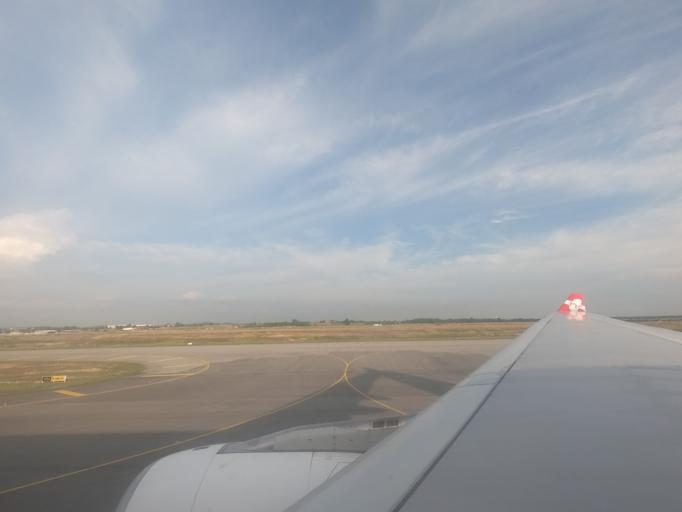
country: MY
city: Sungai Pelek New Village
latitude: 2.7371
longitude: 101.6883
